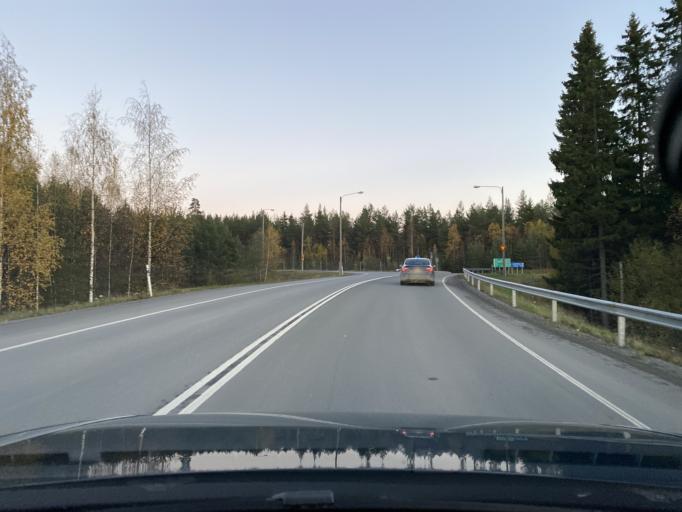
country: FI
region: Pirkanmaa
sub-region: Tampere
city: Lempaeaelae
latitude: 61.3266
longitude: 23.7746
